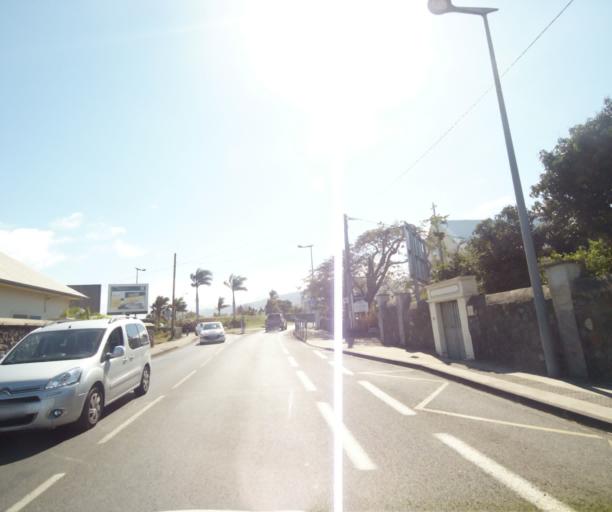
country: RE
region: Reunion
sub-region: Reunion
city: Saint-Paul
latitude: -20.9856
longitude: 55.2978
